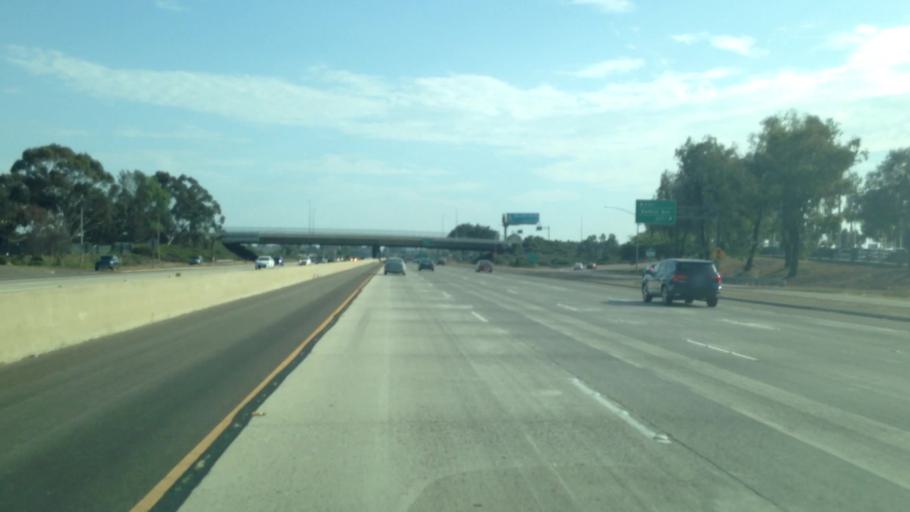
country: US
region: California
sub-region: San Diego County
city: San Diego
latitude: 32.8247
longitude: -117.1451
